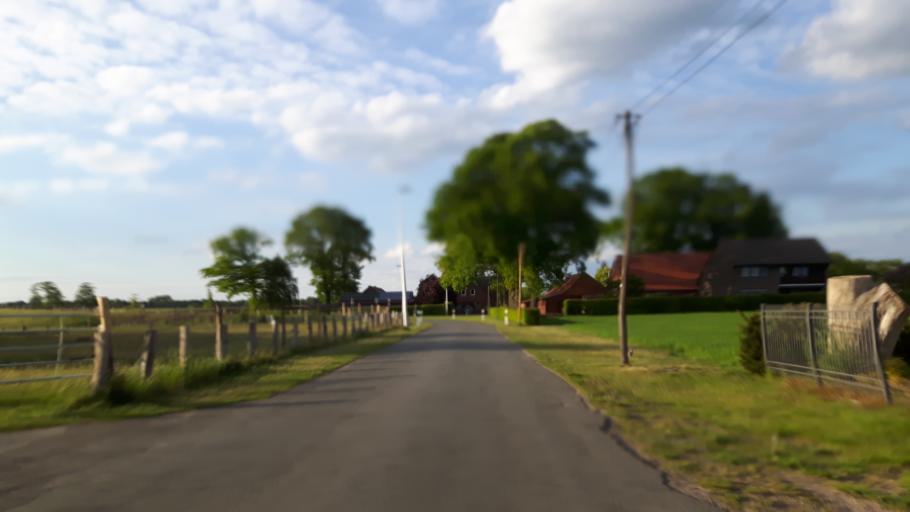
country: DE
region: Lower Saxony
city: Delmenhorst
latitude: 53.0237
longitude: 8.6015
